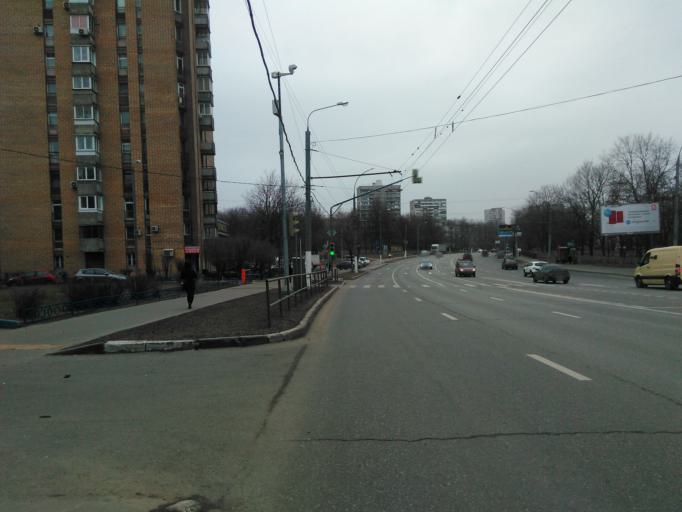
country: RU
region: Moscow
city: Kotlovka
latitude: 55.6515
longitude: 37.5889
